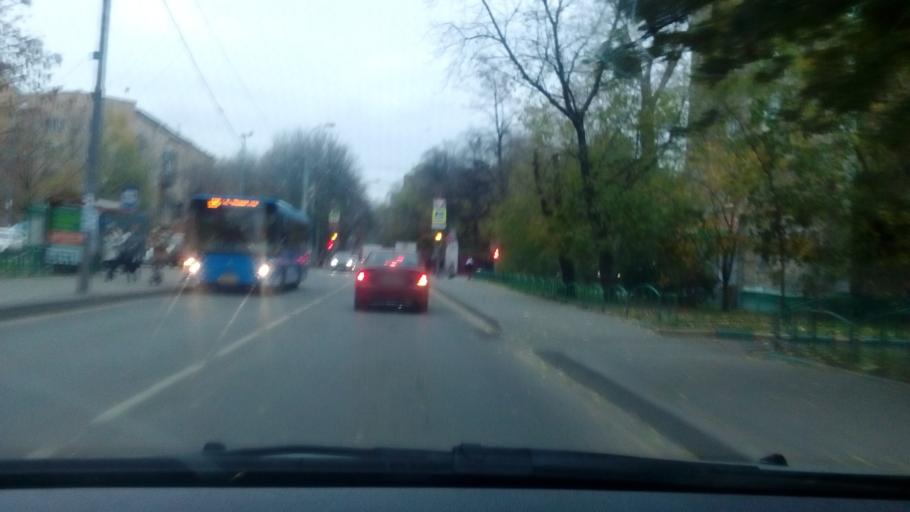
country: RU
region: Moscow
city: Sokol
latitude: 55.7997
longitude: 37.5585
